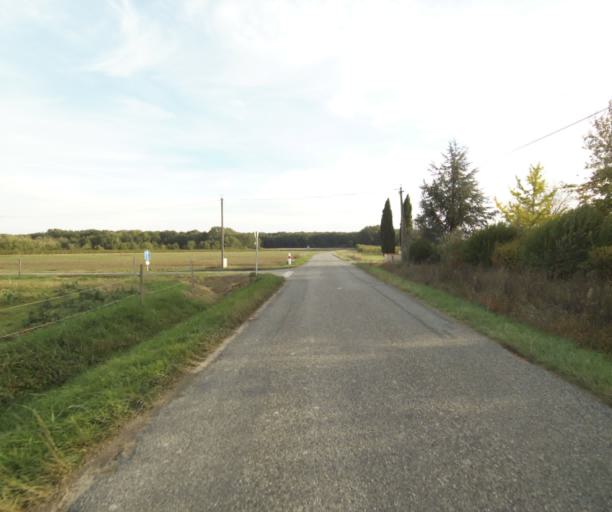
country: FR
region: Midi-Pyrenees
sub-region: Departement du Tarn-et-Garonne
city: Campsas
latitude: 43.8764
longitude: 1.3401
